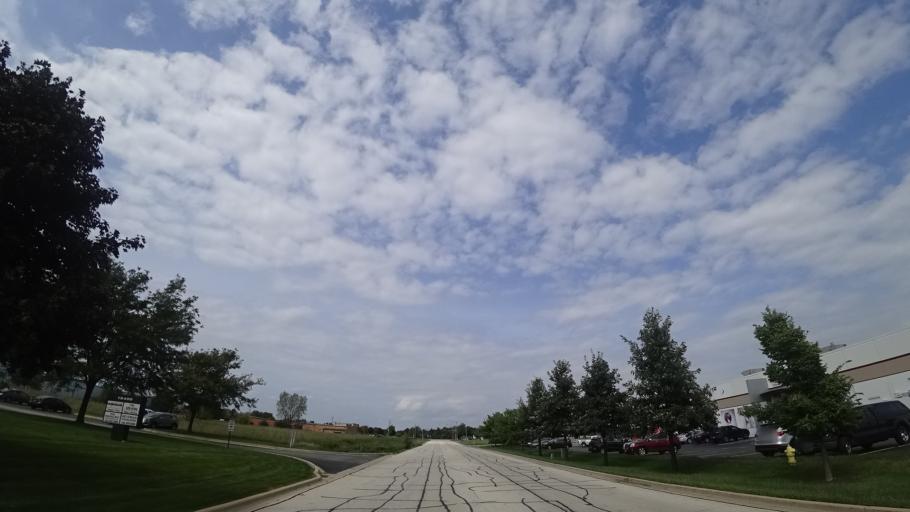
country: US
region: Illinois
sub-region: Cook County
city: Tinley Park
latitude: 41.5562
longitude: -87.8024
